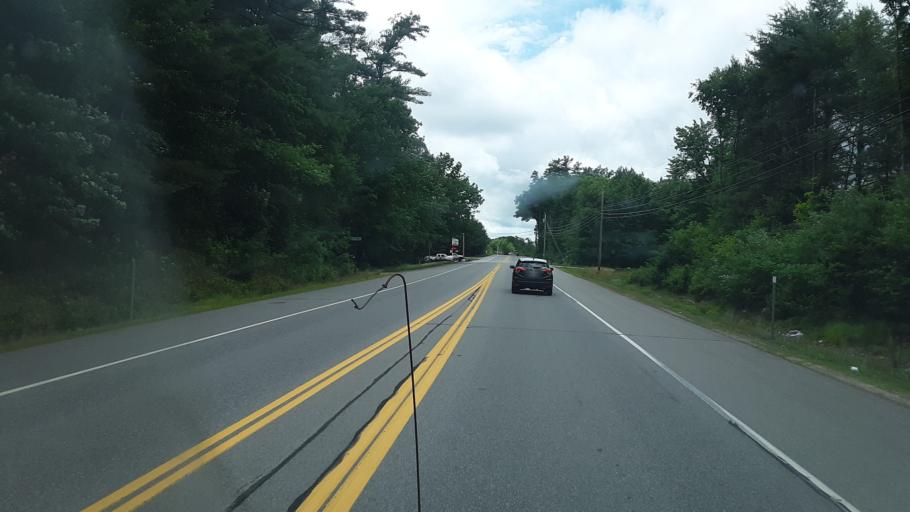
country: US
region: New Hampshire
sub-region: Merrimack County
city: Epsom
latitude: 43.2230
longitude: -71.2589
